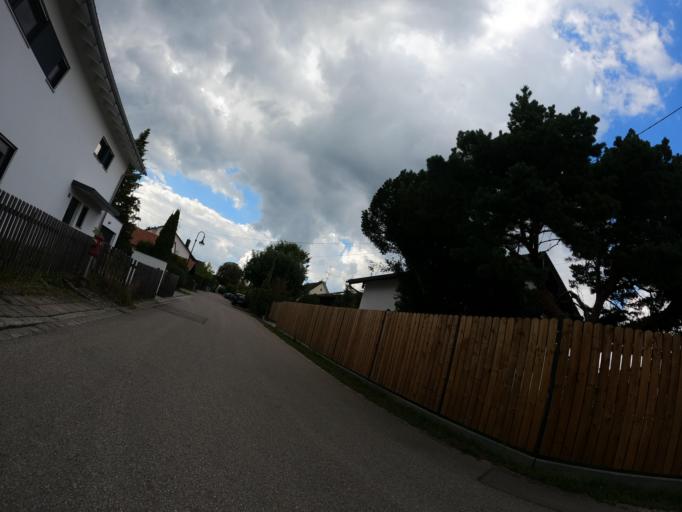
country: DE
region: Bavaria
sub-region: Upper Bavaria
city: Brunnthal
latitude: 48.0049
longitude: 11.6828
